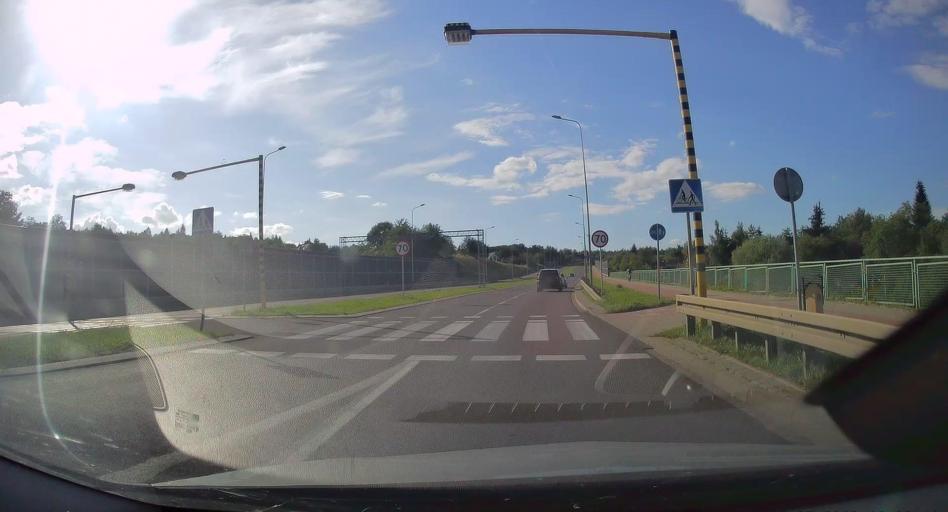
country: PL
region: Subcarpathian Voivodeship
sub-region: Przemysl
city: Przemysl
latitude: 49.8002
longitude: 22.7818
